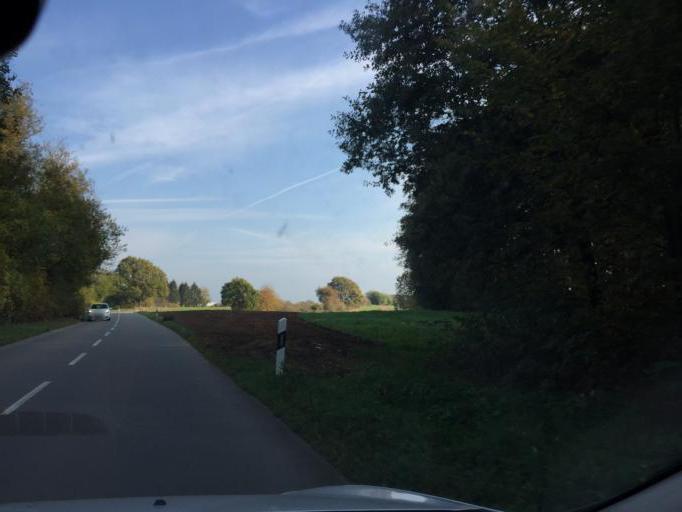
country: LU
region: Luxembourg
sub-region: Canton de Luxembourg
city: Contern
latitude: 49.5721
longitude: 6.2171
